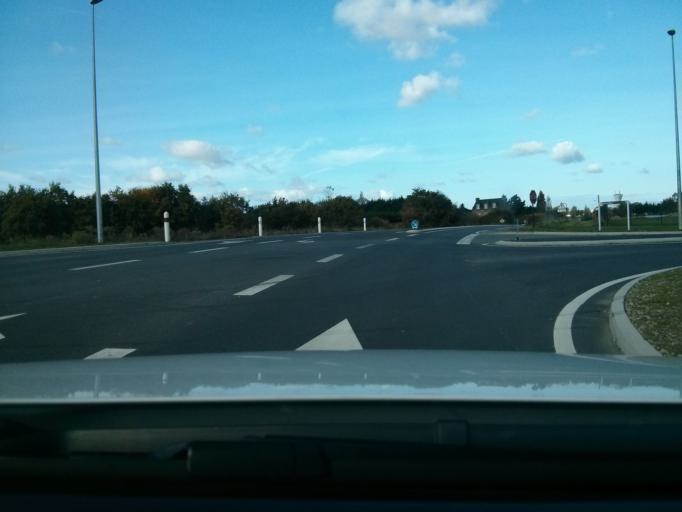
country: FR
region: Brittany
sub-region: Departement des Cotes-d'Armor
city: Pleslin-Trigavou
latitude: 48.5219
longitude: -2.0443
